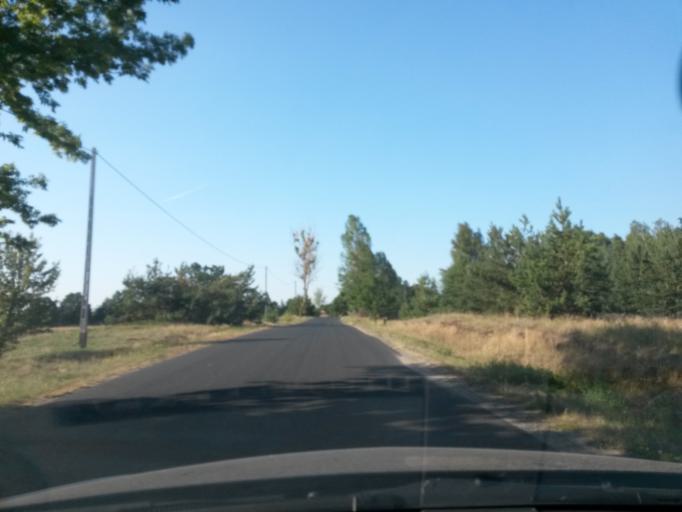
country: PL
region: Kujawsko-Pomorskie
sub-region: Powiat brodnicki
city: Gorzno
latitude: 53.1727
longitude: 19.6381
